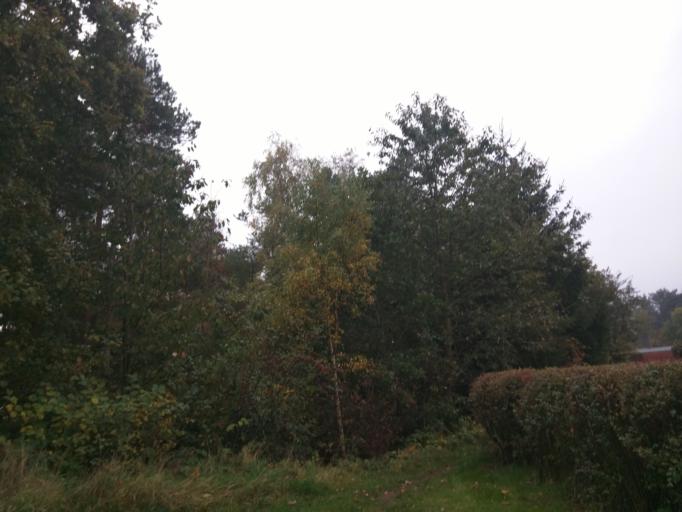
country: DK
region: Central Jutland
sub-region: Silkeborg Kommune
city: Silkeborg
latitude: 56.1897
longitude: 9.5354
